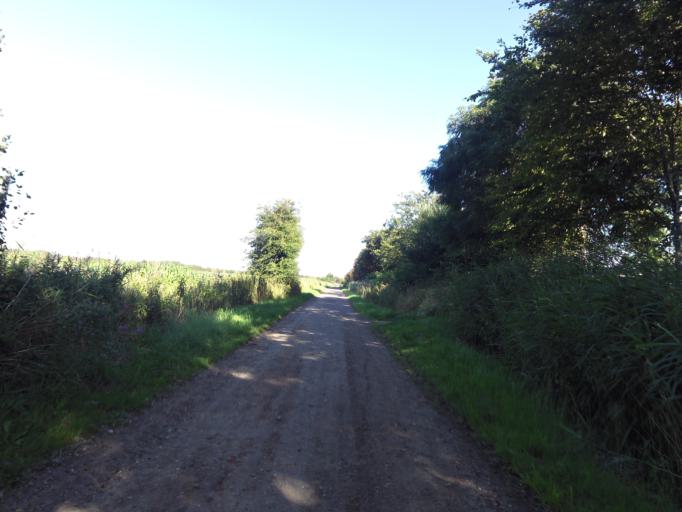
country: DK
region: South Denmark
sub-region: Tonder Kommune
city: Sherrebek
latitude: 55.1556
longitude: 8.7454
